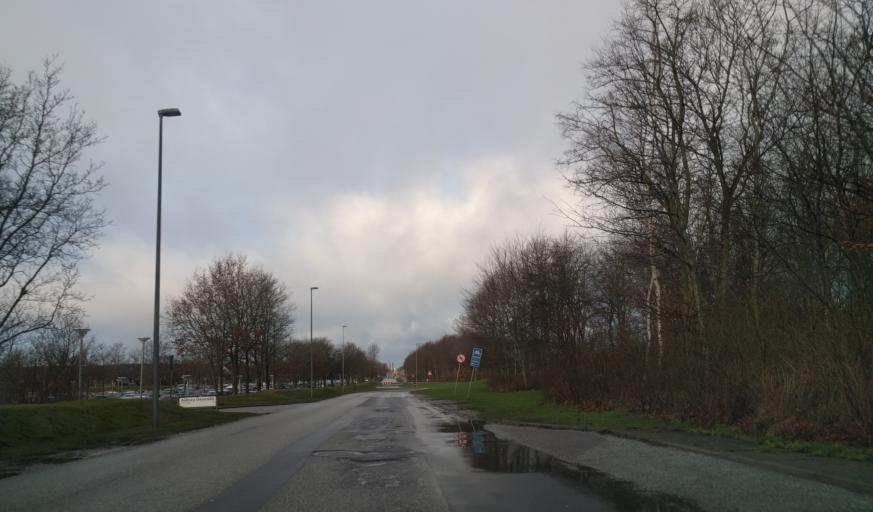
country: DK
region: North Denmark
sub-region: Alborg Kommune
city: Gistrup
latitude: 57.0186
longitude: 9.9790
